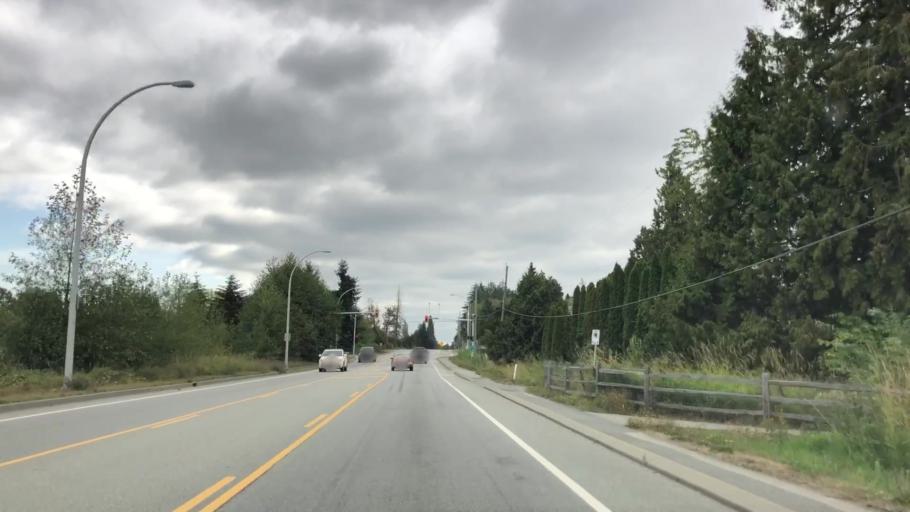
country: CA
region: British Columbia
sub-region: Greater Vancouver Regional District
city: White Rock
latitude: 49.0603
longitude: -122.7588
